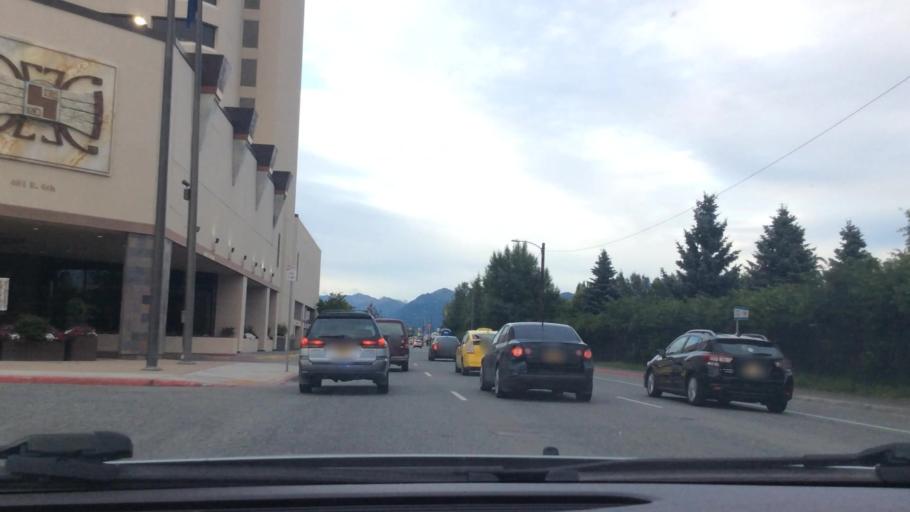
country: US
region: Alaska
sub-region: Anchorage Municipality
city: Anchorage
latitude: 61.2166
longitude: -149.8774
